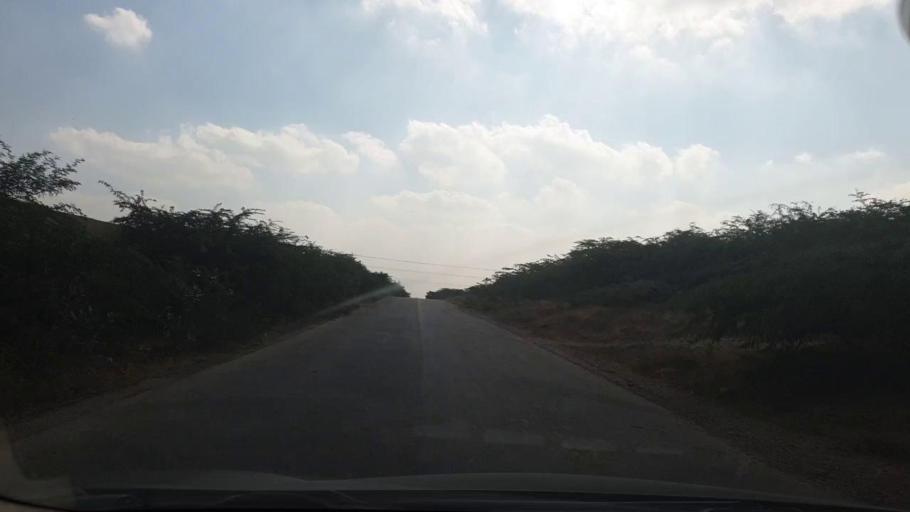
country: PK
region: Sindh
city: Malir Cantonment
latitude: 25.0129
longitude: 67.3531
